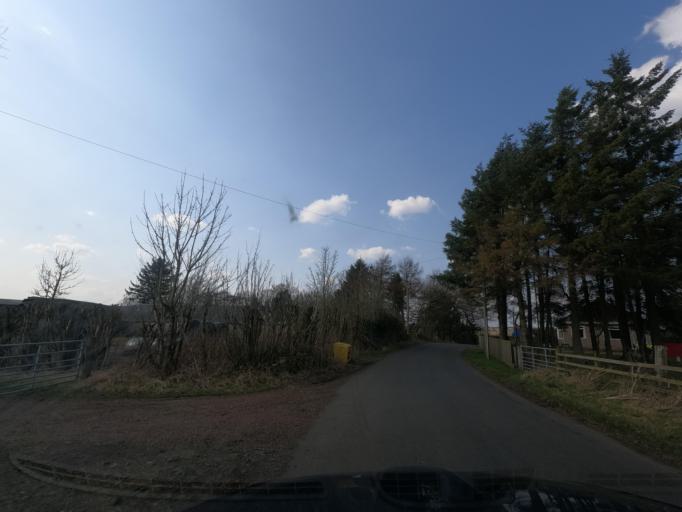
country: GB
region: Scotland
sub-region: South Lanarkshire
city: Forth
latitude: 55.7558
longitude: -3.6591
